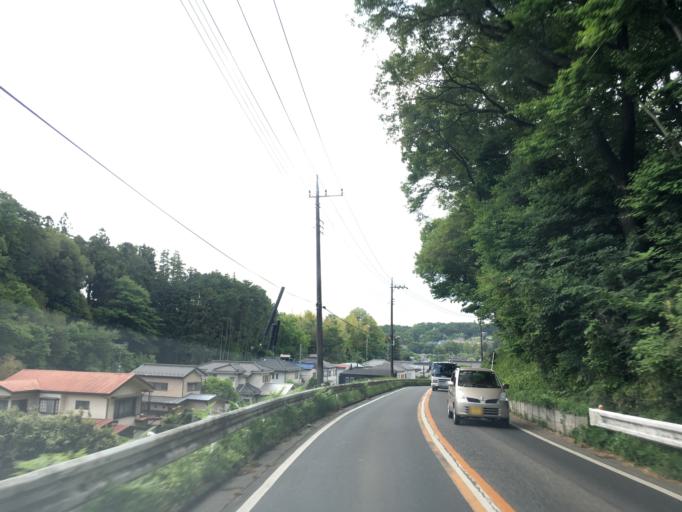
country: JP
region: Saitama
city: Tokorozawa
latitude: 35.7817
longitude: 139.4173
